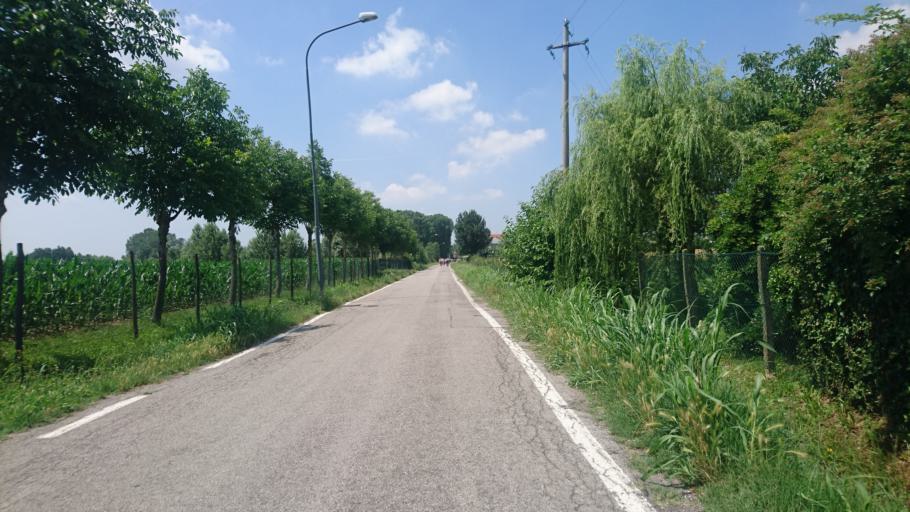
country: IT
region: Veneto
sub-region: Provincia di Venezia
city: Fiesso
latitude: 45.4160
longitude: 12.0503
